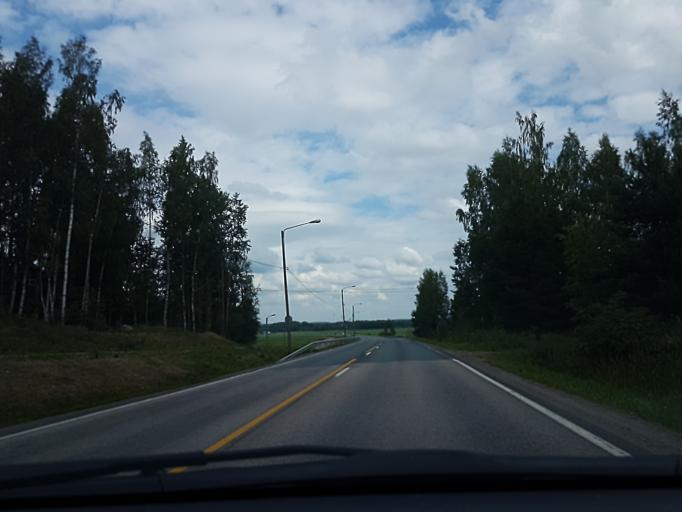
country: FI
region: Uusimaa
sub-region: Helsinki
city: Jaervenpaeae
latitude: 60.5078
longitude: 25.0998
